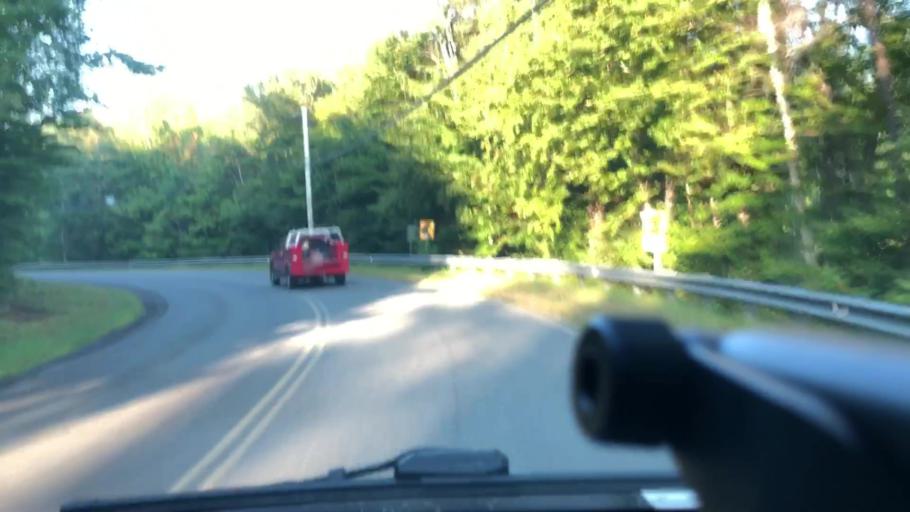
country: US
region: Massachusetts
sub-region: Franklin County
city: Ashfield
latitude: 42.5116
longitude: -72.8216
